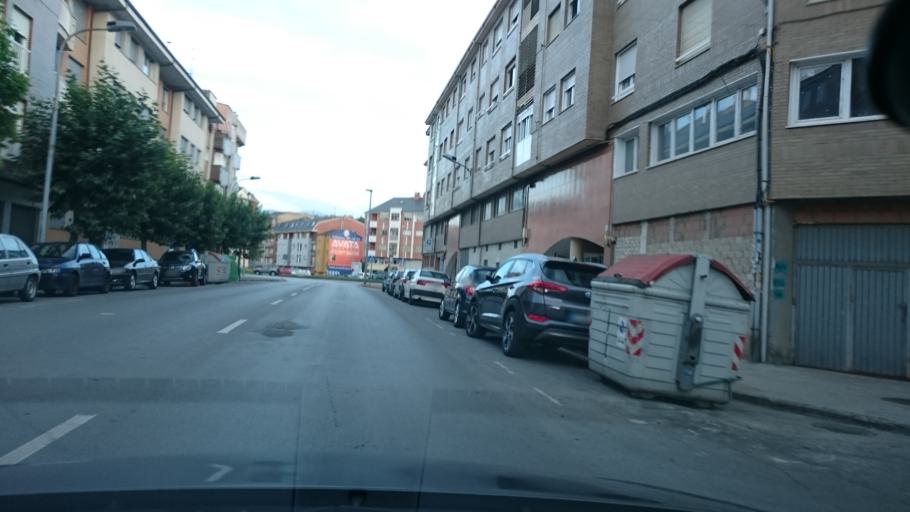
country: ES
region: Castille and Leon
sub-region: Provincia de Leon
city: Ponferrada
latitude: 42.5435
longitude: -6.6004
